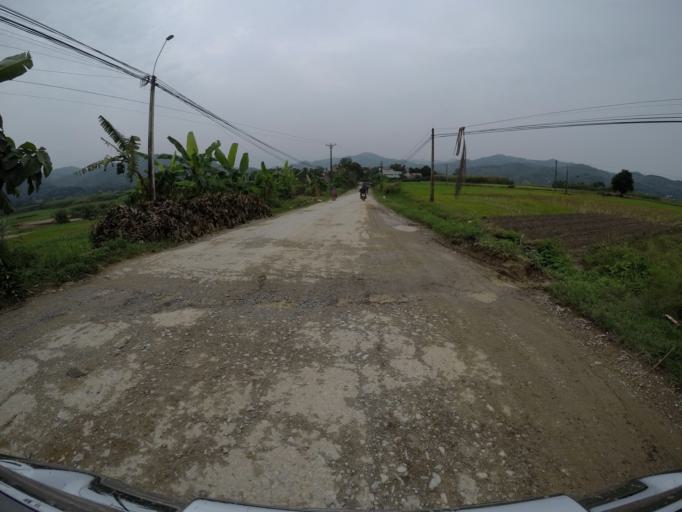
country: VN
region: Yen Bai
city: Co Phuc
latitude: 21.8657
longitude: 104.6483
